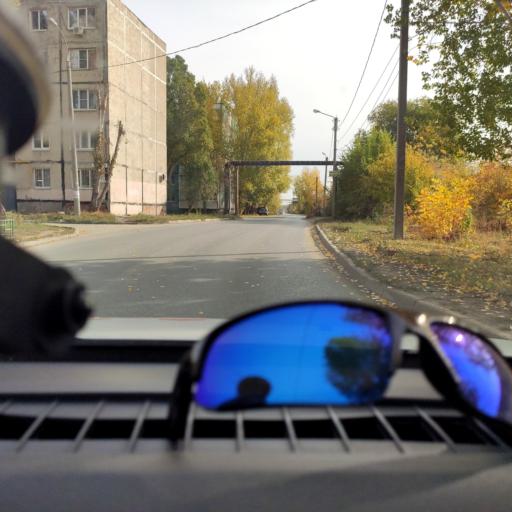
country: RU
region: Samara
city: Samara
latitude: 53.1201
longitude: 50.0931
